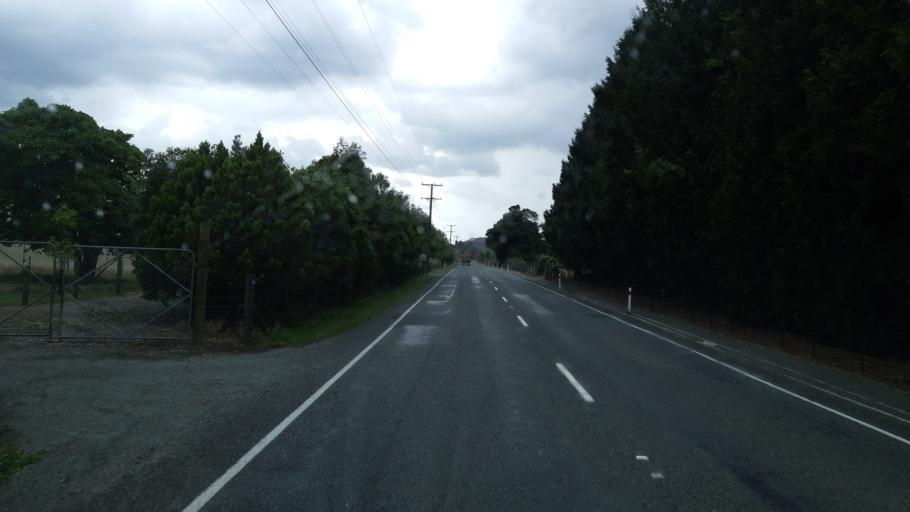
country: NZ
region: Tasman
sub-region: Tasman District
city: Wakefield
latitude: -41.4261
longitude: 172.9962
